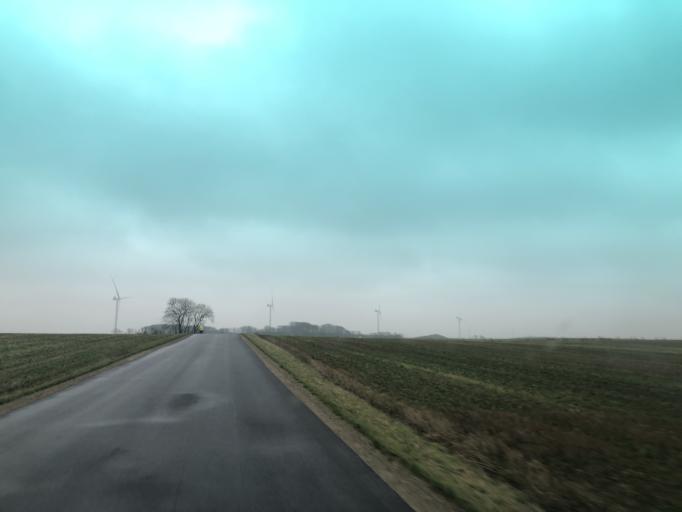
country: DK
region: Central Jutland
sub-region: Struer Kommune
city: Struer
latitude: 56.4329
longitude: 8.5885
